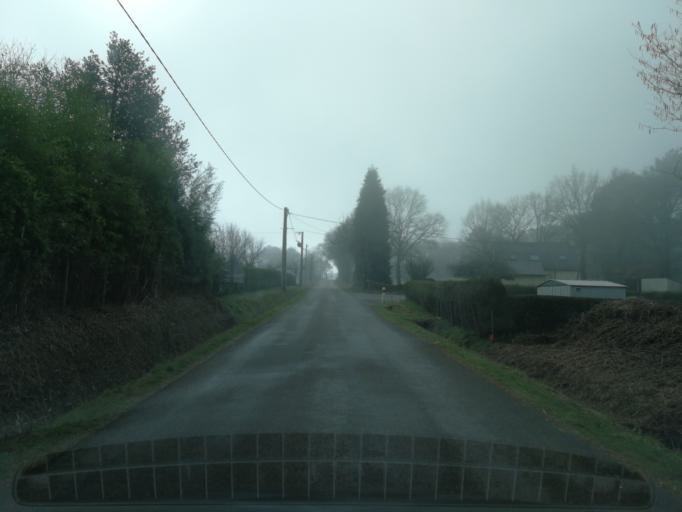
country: FR
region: Brittany
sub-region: Departement du Morbihan
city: La Vraie-Croix
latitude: 47.7201
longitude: -2.5123
